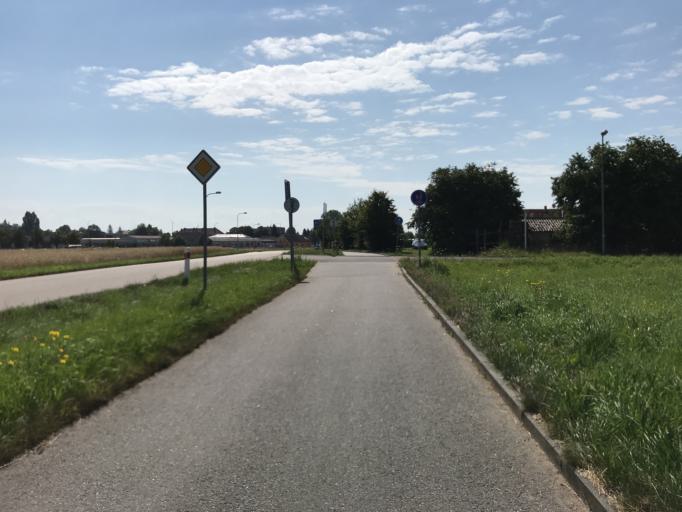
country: CZ
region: Jihocesky
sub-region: Okres Jindrichuv Hradec
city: Trebon
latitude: 49.0149
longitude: 14.7523
